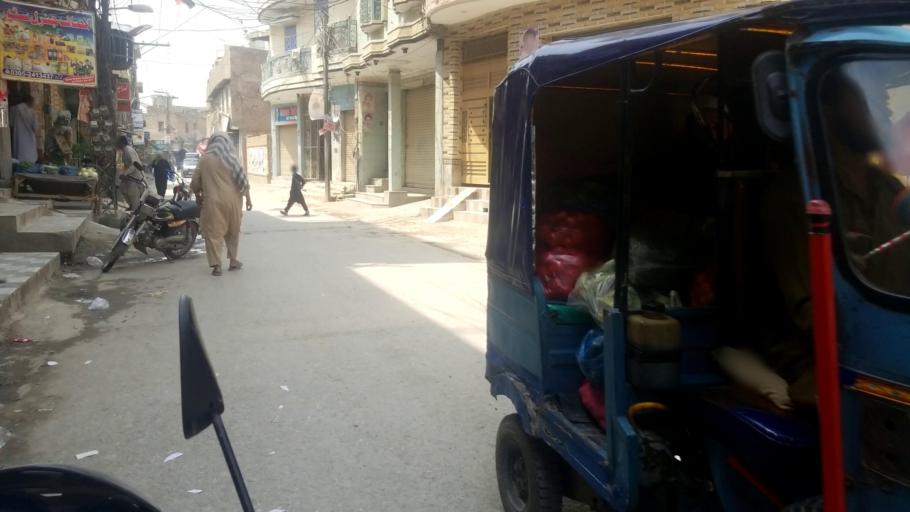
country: PK
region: Khyber Pakhtunkhwa
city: Peshawar
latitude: 34.0269
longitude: 71.5819
